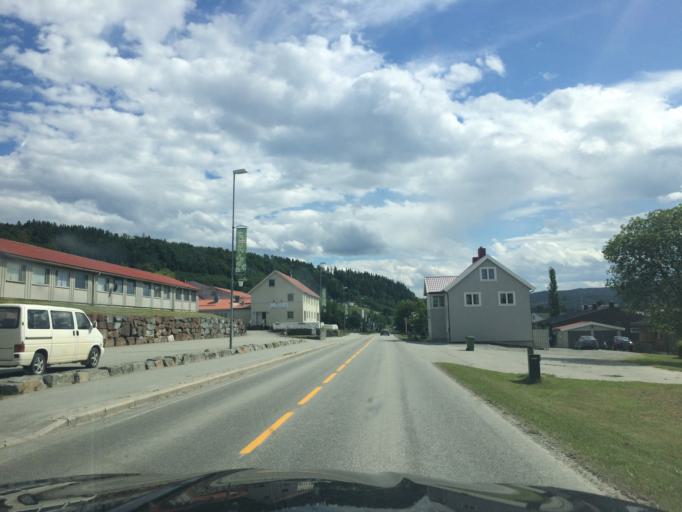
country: NO
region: Sor-Trondelag
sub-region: Selbu
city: Mebonden
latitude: 63.2215
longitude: 11.0373
